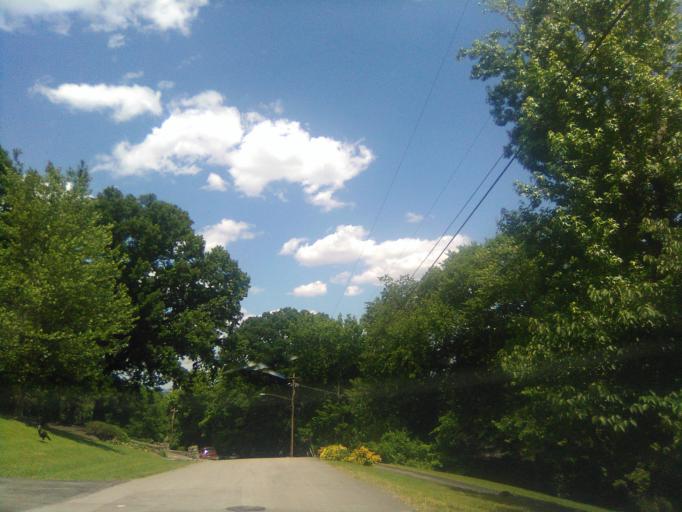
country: US
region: Tennessee
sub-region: Davidson County
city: Belle Meade
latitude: 36.1347
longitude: -86.8667
